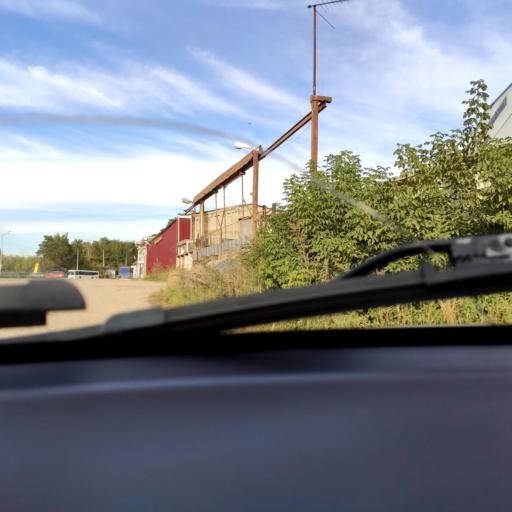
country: RU
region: Tatarstan
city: Staroye Arakchino
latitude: 55.8358
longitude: 49.0264
